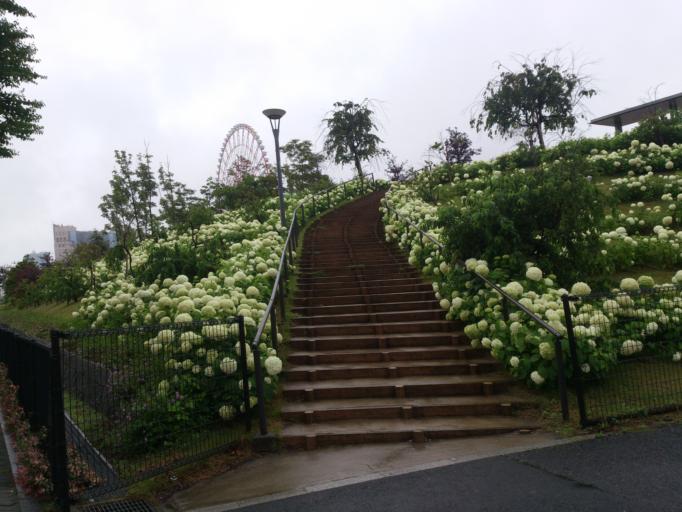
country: JP
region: Tokyo
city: Tokyo
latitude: 35.6252
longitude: 139.7773
